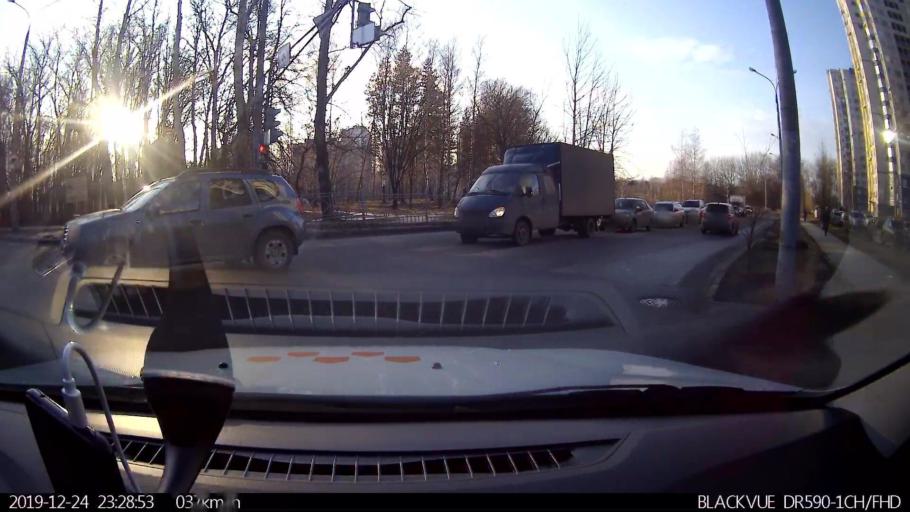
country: RU
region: Nizjnij Novgorod
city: Gorbatovka
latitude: 56.2401
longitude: 43.8486
